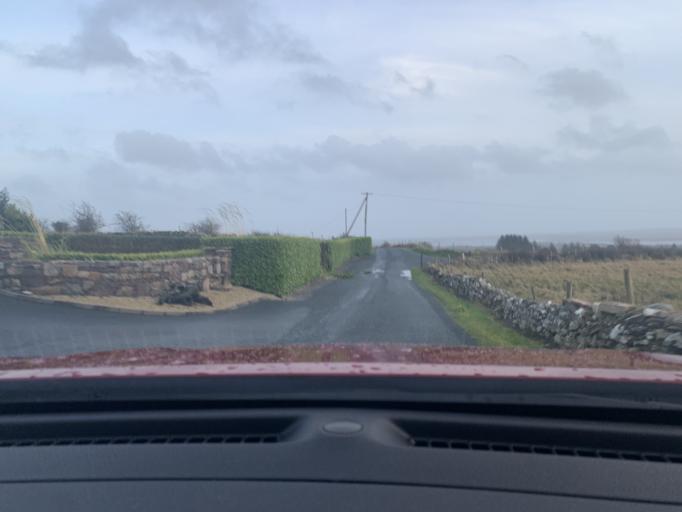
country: IE
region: Connaught
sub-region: Roscommon
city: Ballaghaderreen
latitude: 53.9484
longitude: -8.5111
